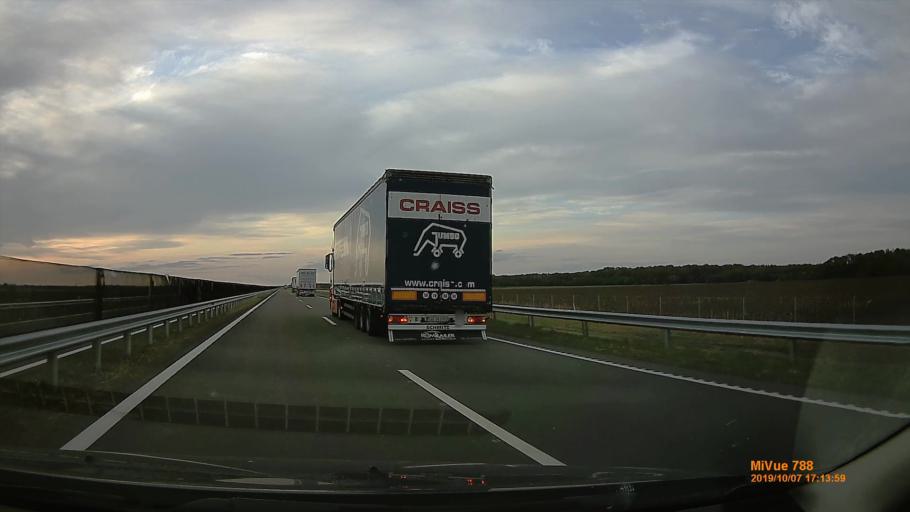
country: HU
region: Jasz-Nagykun-Szolnok
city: Kunszentmarton
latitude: 46.8272
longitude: 20.3602
